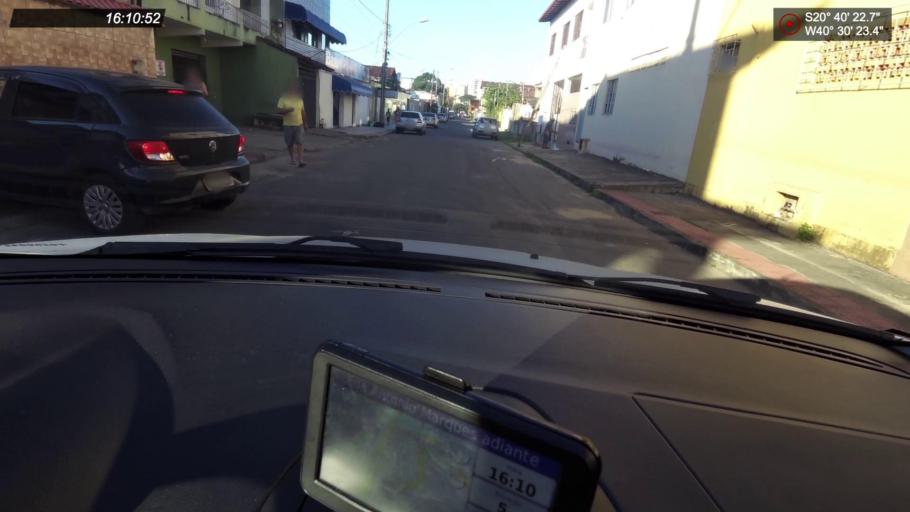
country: BR
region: Espirito Santo
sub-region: Guarapari
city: Guarapari
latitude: -20.6730
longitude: -40.5065
